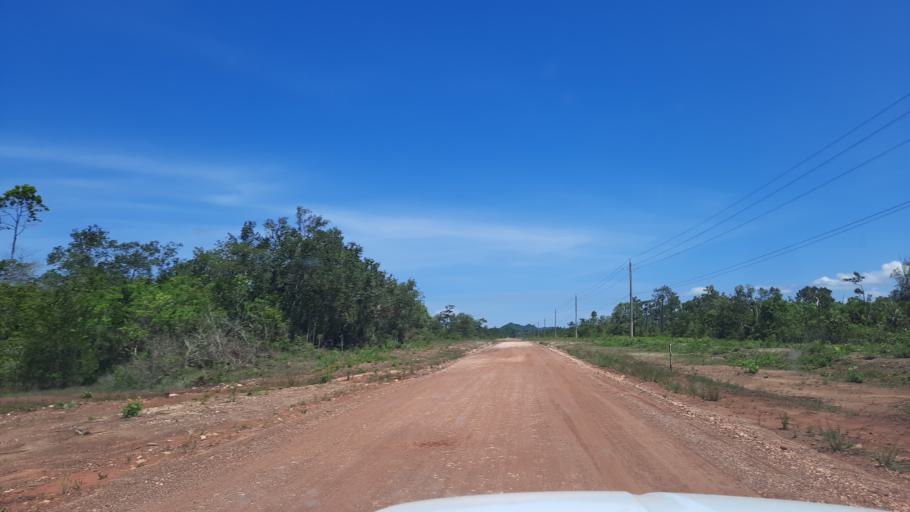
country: BZ
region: Stann Creek
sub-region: Dangriga
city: Dangriga
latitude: 17.2373
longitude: -88.4165
